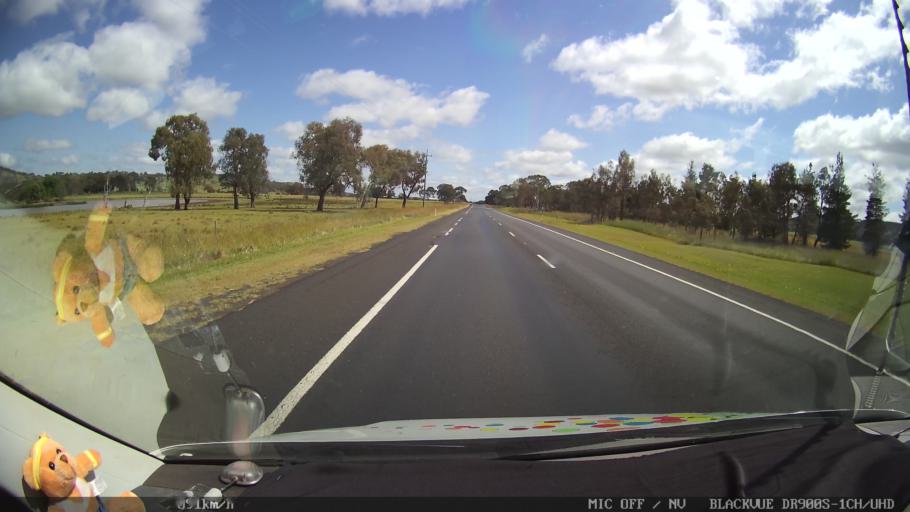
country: AU
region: New South Wales
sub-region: Glen Innes Severn
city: Glen Innes
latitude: -29.8743
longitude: 151.7348
